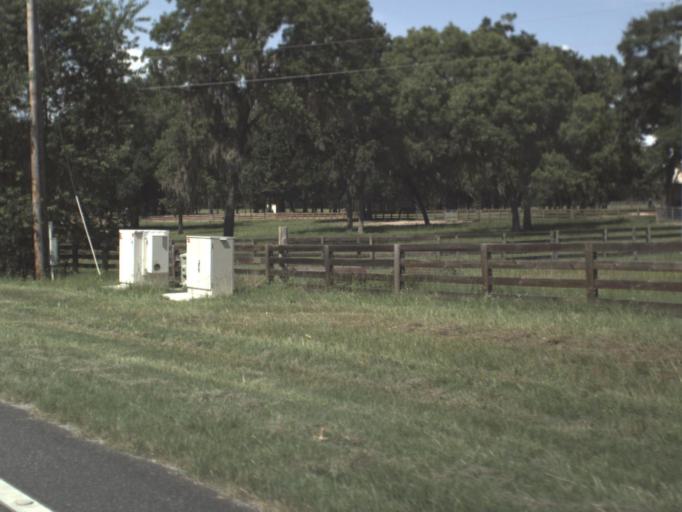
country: US
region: Florida
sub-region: Alachua County
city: High Springs
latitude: 29.8732
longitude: -82.7365
